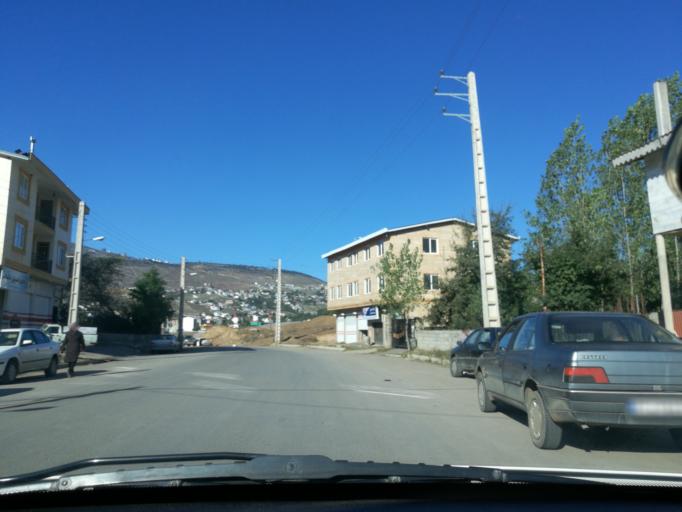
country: IR
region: Mazandaran
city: `Abbasabad
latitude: 36.5402
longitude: 51.1815
